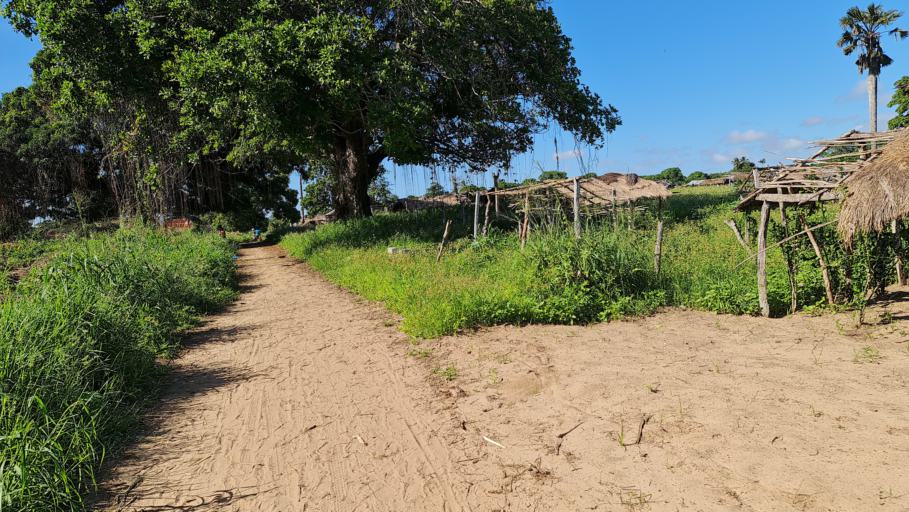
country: MZ
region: Zambezia
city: Quelimane
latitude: -17.4424
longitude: 37.6988
